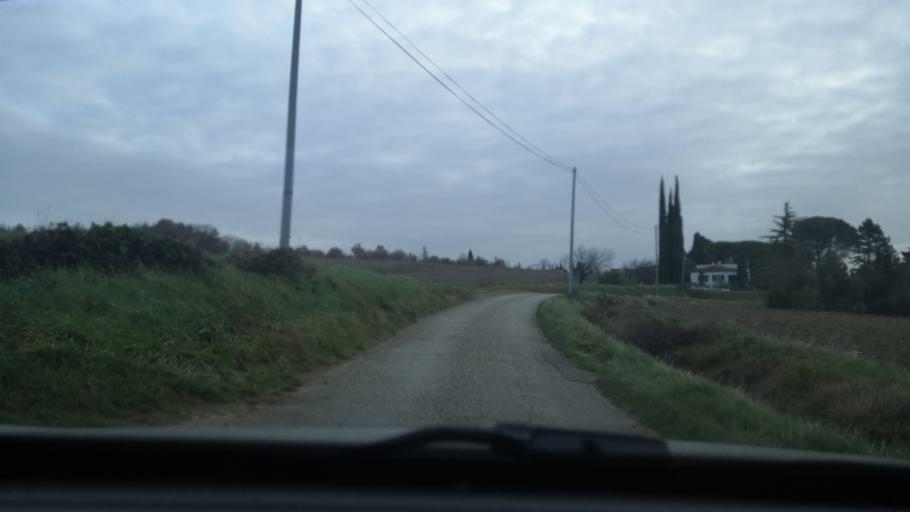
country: FR
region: Rhone-Alpes
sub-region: Departement de la Drome
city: Sauzet
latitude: 44.5635
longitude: 4.8618
